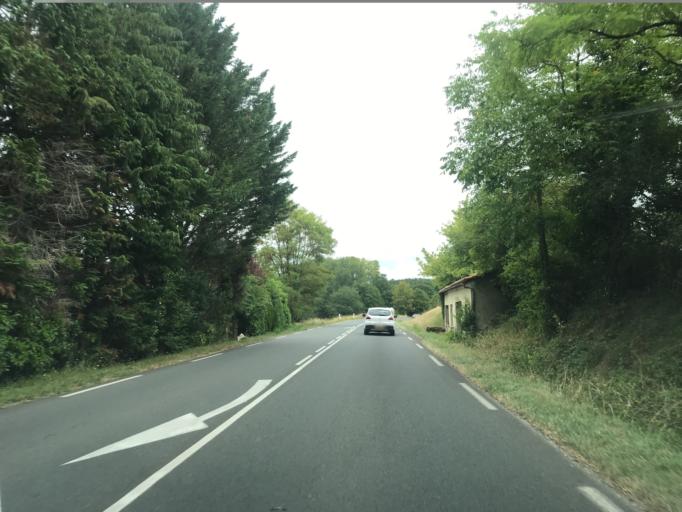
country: FR
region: Aquitaine
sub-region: Departement de la Dordogne
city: Mareuil
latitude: 45.4694
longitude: 0.4350
